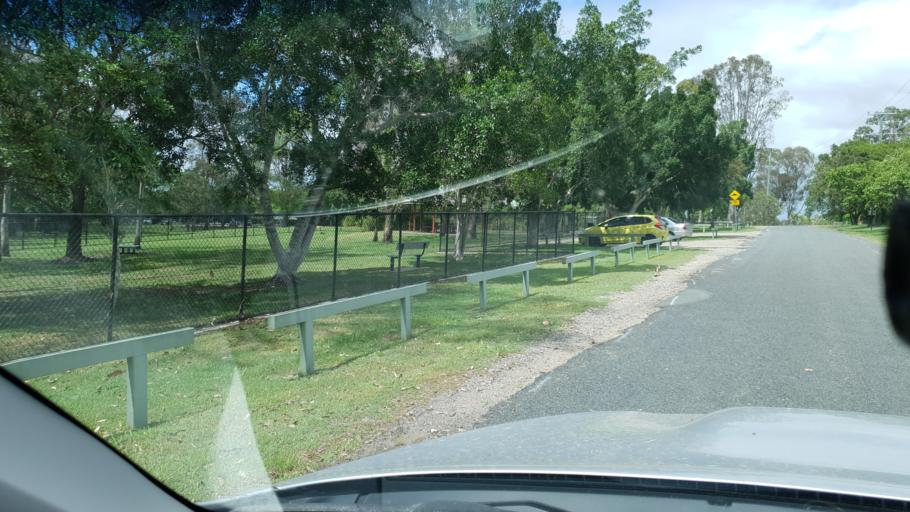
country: AU
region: Queensland
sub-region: Gold Coast
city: Yatala
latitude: -27.6789
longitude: 153.2272
